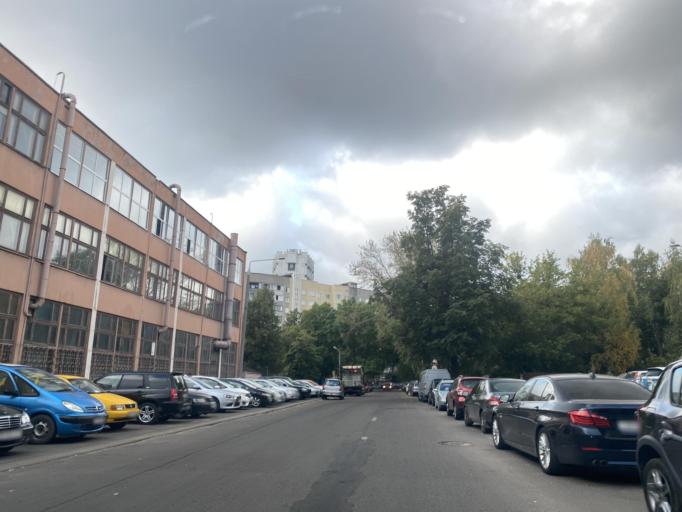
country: BY
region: Minsk
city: Minsk
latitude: 53.9201
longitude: 27.5623
